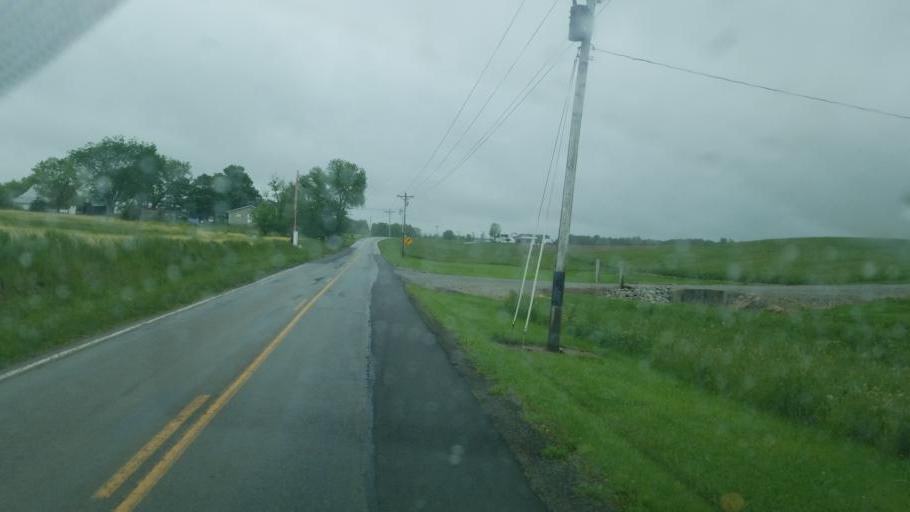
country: US
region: Ohio
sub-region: Highland County
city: Greenfield
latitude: 39.3387
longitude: -83.4521
